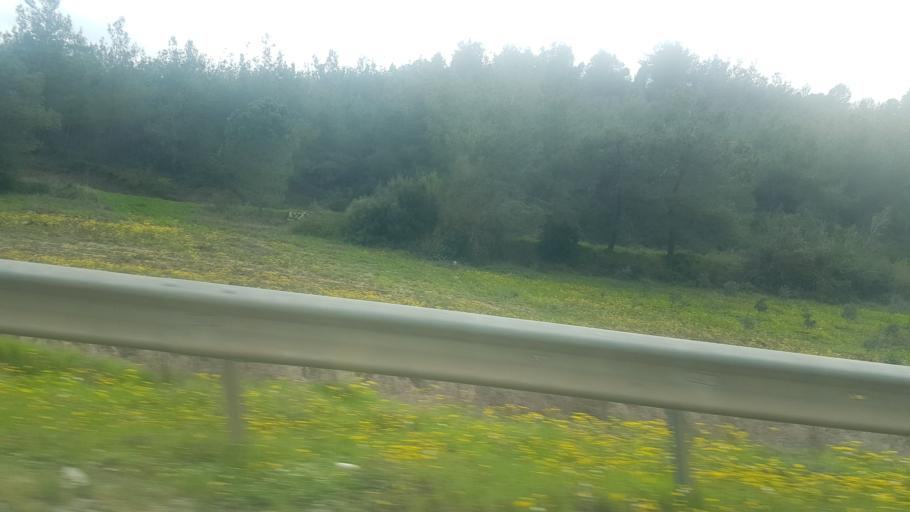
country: TR
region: Mersin
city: Yenice
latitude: 37.0864
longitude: 35.1647
